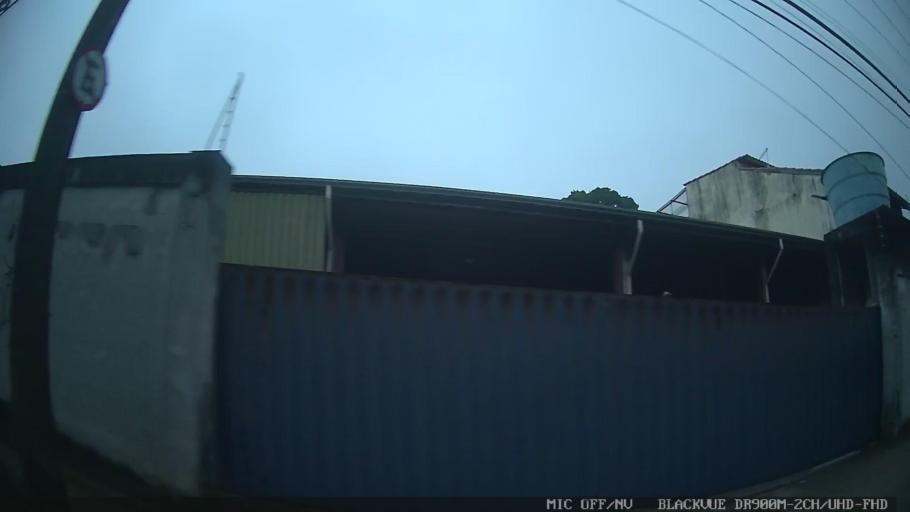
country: BR
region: Sao Paulo
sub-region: Mogi das Cruzes
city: Mogi das Cruzes
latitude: -23.5036
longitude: -46.1940
